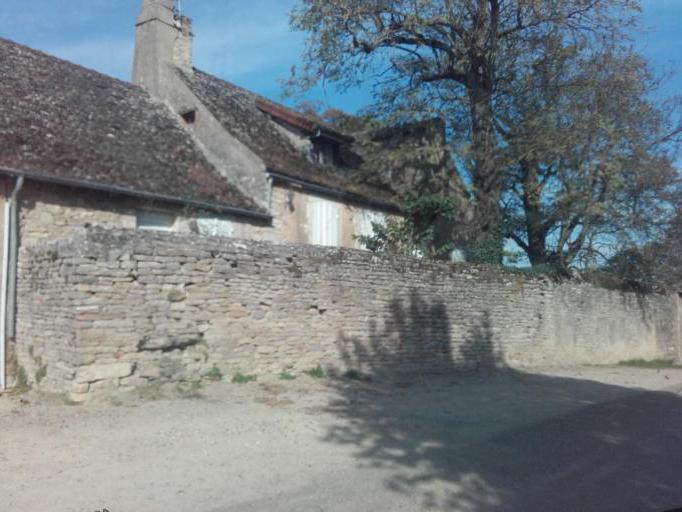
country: FR
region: Bourgogne
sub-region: Departement de Saone-et-Loire
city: Mellecey
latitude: 46.8293
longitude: 4.7150
